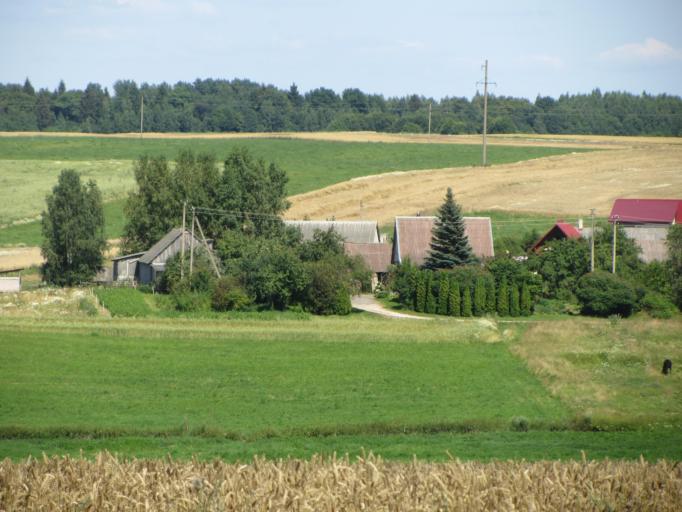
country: LT
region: Vilnius County
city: Ukmerge
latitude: 55.0749
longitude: 24.7592
